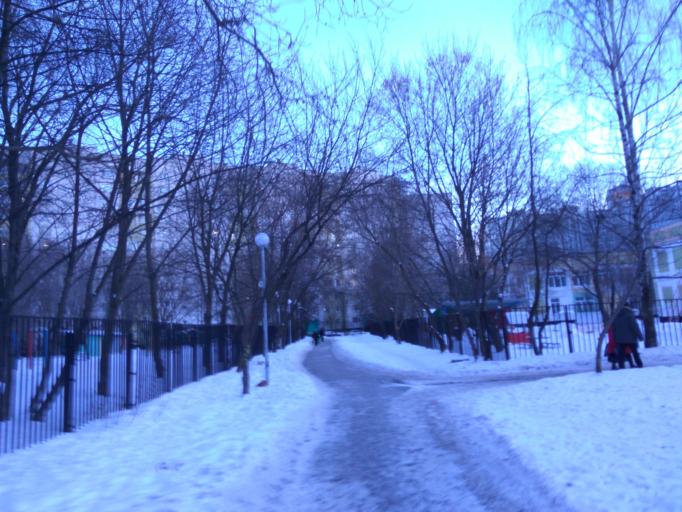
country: RU
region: Moscow
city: Biryulevo
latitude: 55.5856
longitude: 37.6702
